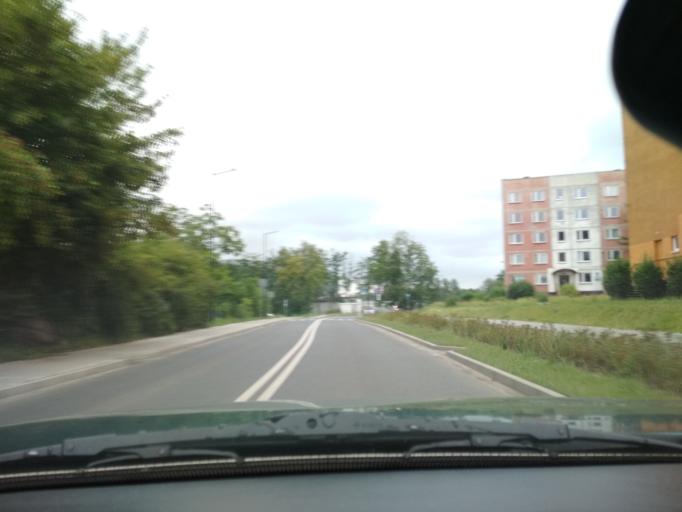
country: PL
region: Silesian Voivodeship
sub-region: Gliwice
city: Gliwice
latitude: 50.2864
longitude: 18.6798
